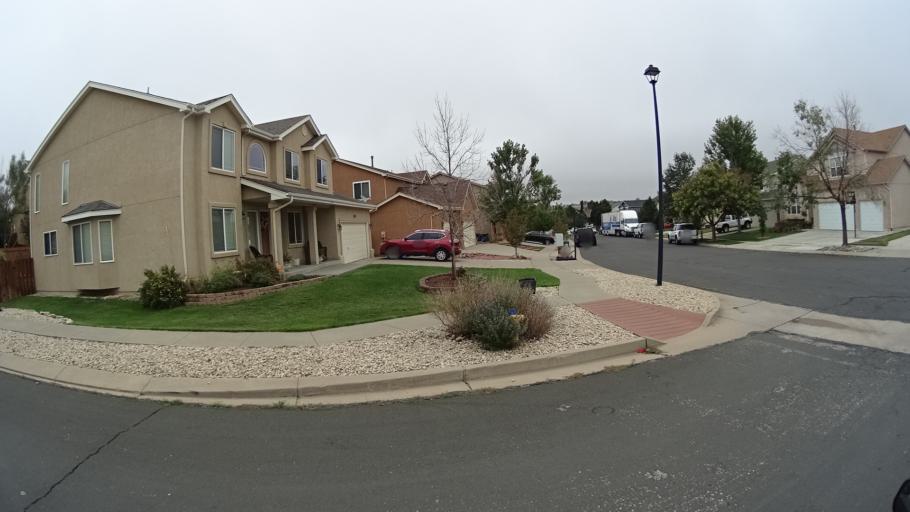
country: US
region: Colorado
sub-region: El Paso County
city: Cimarron Hills
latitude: 38.9324
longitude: -104.7452
